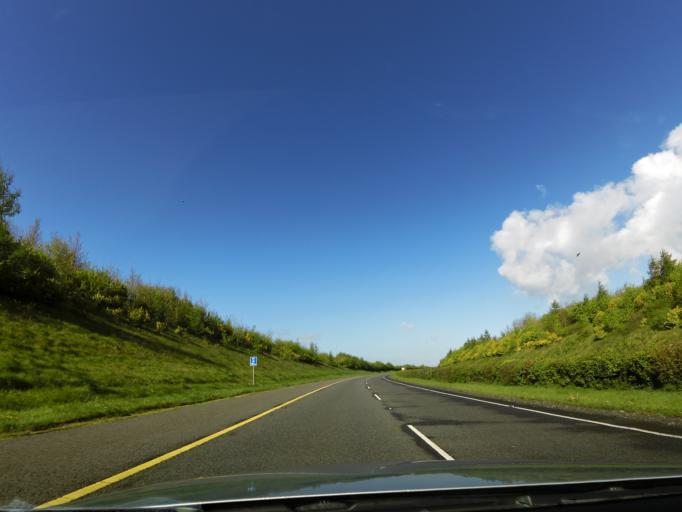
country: IE
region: Munster
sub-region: County Limerick
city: Luimneach
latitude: 52.6386
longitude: -8.5901
